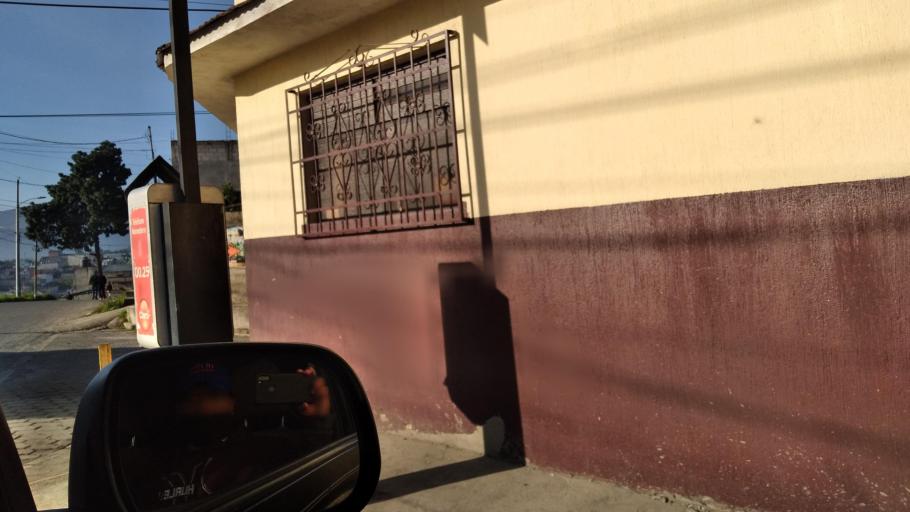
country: GT
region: Quetzaltenango
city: Quetzaltenango
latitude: 14.8541
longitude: -91.5181
